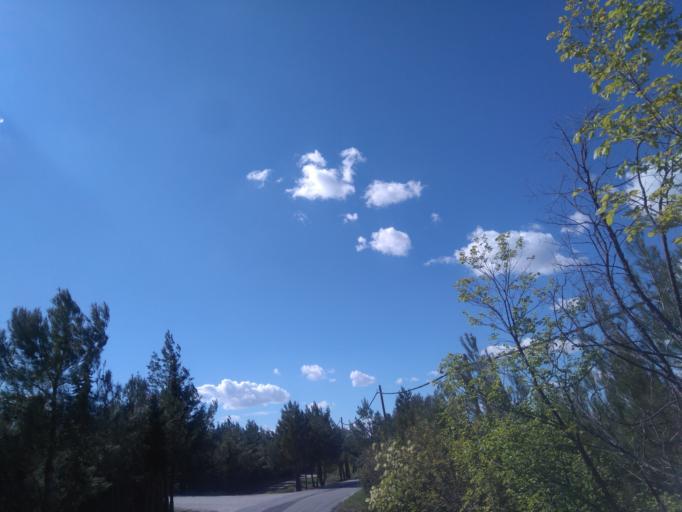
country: GR
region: Central Macedonia
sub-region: Nomos Thessalonikis
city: Asvestochori
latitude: 40.6408
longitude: 23.0077
